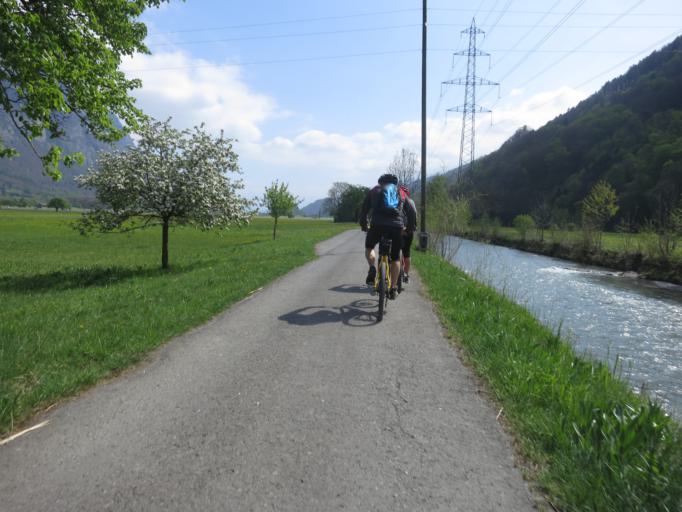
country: CH
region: Saint Gallen
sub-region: Wahlkreis Sarganserland
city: Flums
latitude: 47.0779
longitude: 9.3673
